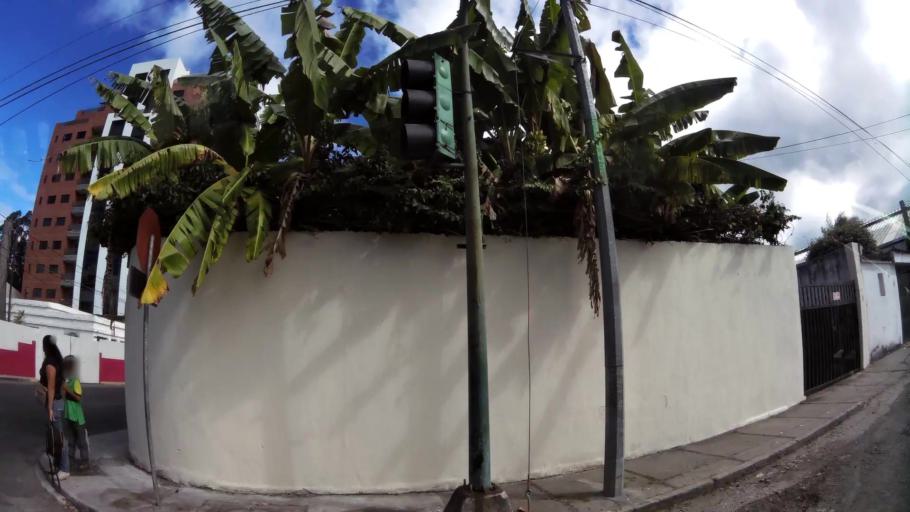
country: GT
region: Guatemala
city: Santa Catarina Pinula
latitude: 14.5920
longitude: -90.5080
